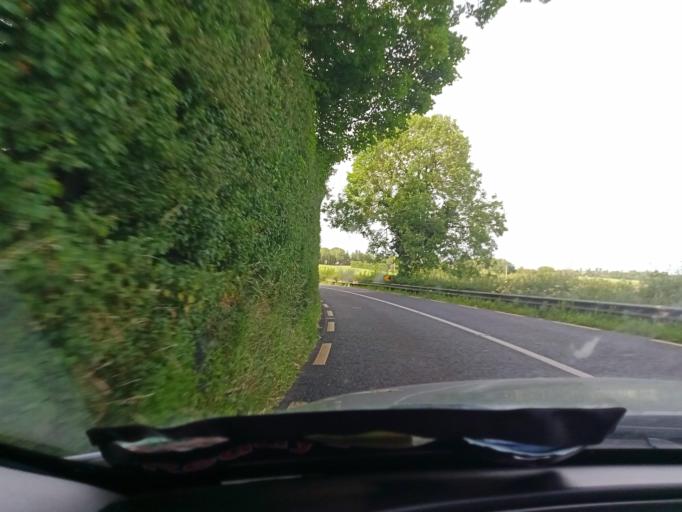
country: IE
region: Leinster
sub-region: An Longfort
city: Granard
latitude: 53.8818
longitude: -7.4394
